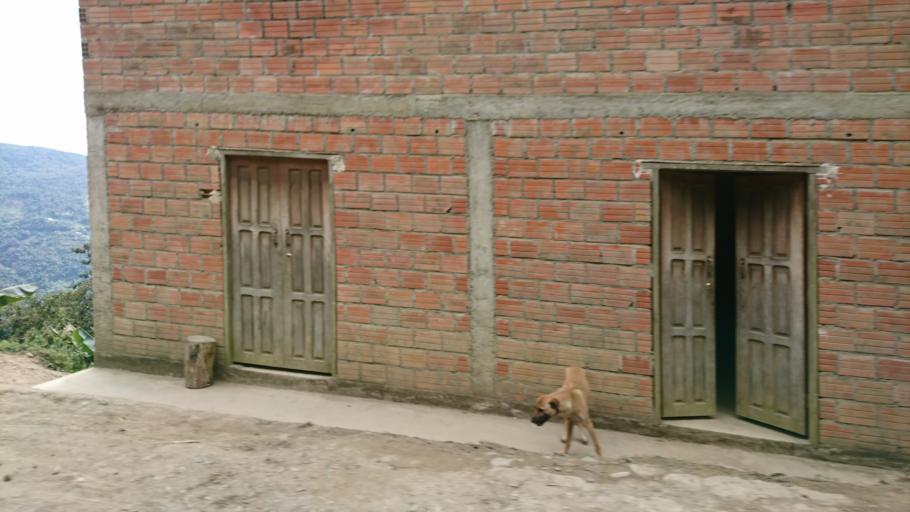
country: BO
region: La Paz
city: Coroico
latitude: -16.1132
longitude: -67.7749
